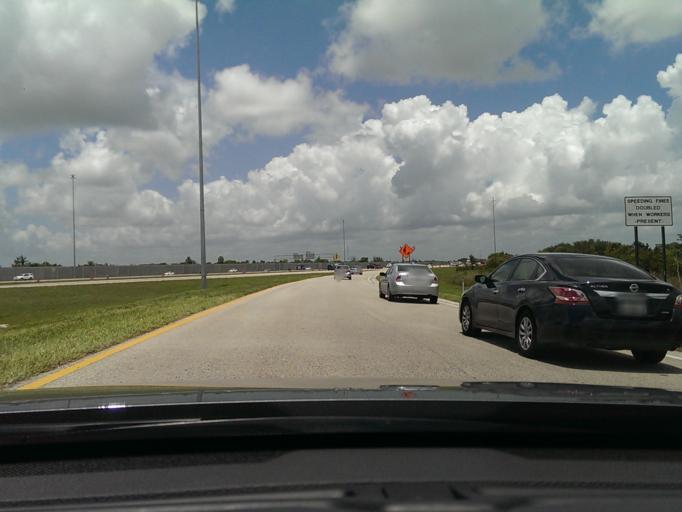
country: US
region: Florida
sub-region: Broward County
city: Sunshine Ranches
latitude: 26.0109
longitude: -80.3407
